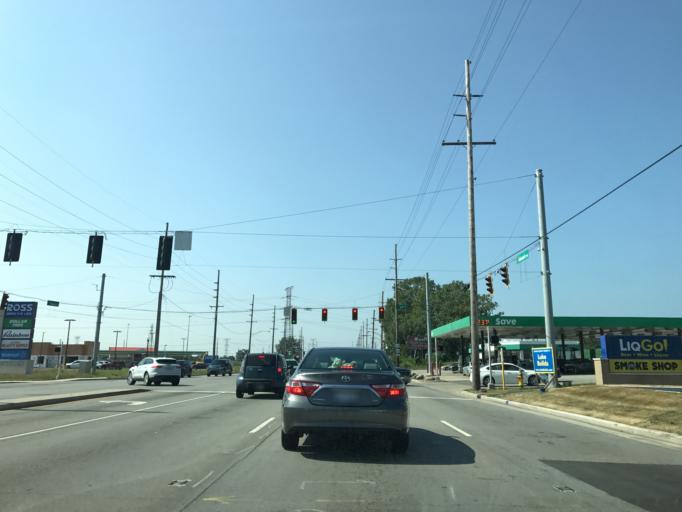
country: US
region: Indiana
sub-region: Lake County
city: Whiting
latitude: 41.6953
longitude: -87.5161
